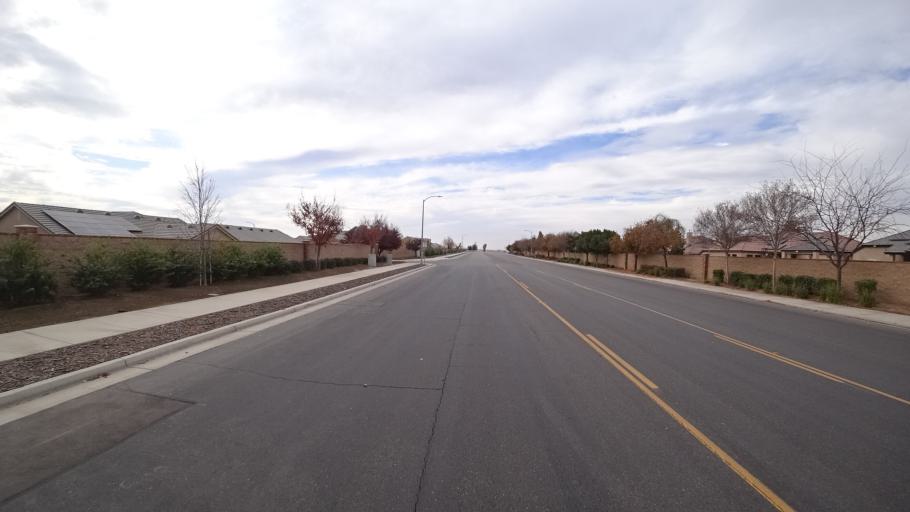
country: US
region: California
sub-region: Kern County
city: Rosedale
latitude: 35.4124
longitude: -119.1487
